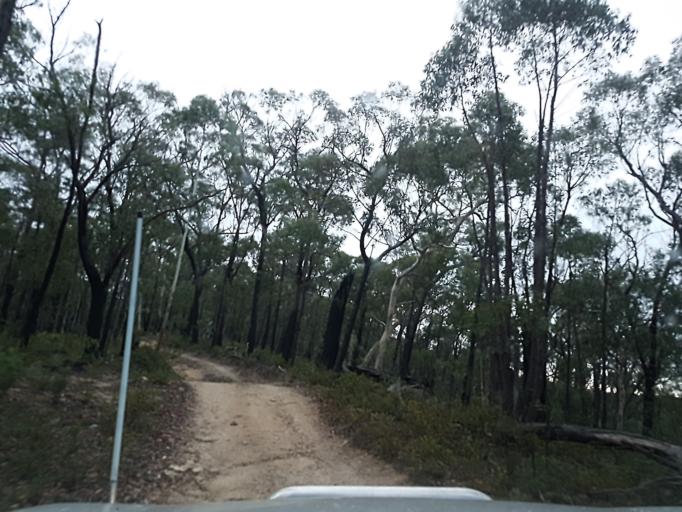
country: AU
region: New South Wales
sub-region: Snowy River
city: Jindabyne
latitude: -36.8532
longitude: 148.2290
